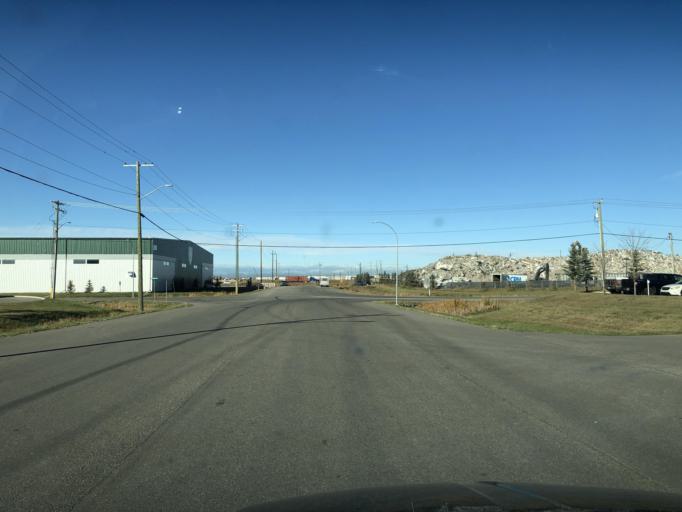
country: CA
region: Alberta
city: Chestermere
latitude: 50.9624
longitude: -113.9074
